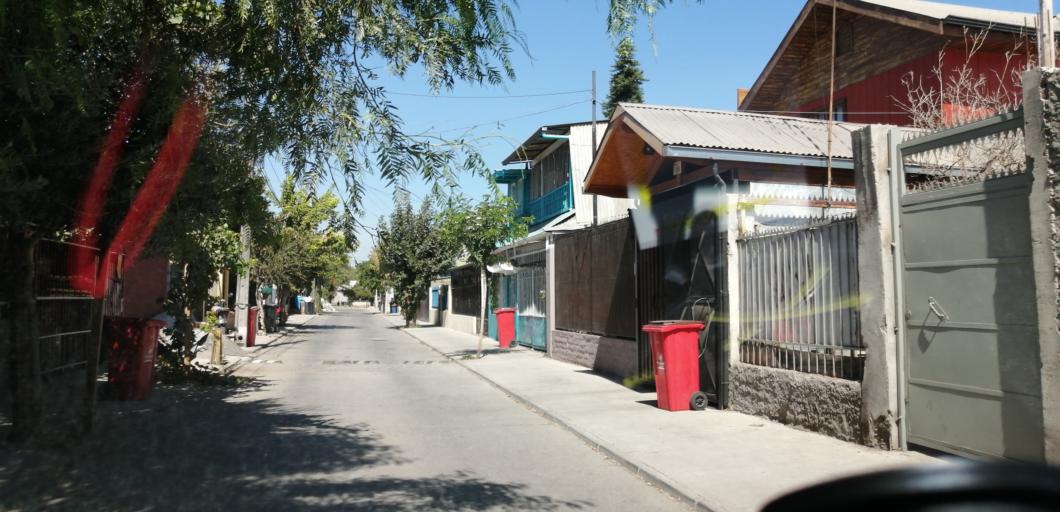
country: CL
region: Santiago Metropolitan
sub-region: Provincia de Santiago
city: Lo Prado
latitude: -33.4336
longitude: -70.7537
